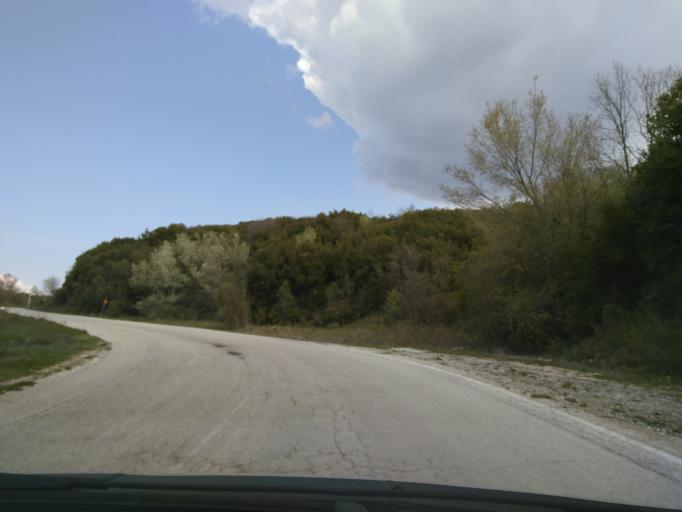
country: GR
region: Epirus
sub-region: Nomos Ioanninon
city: Asprangeloi
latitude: 39.8363
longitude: 20.7064
